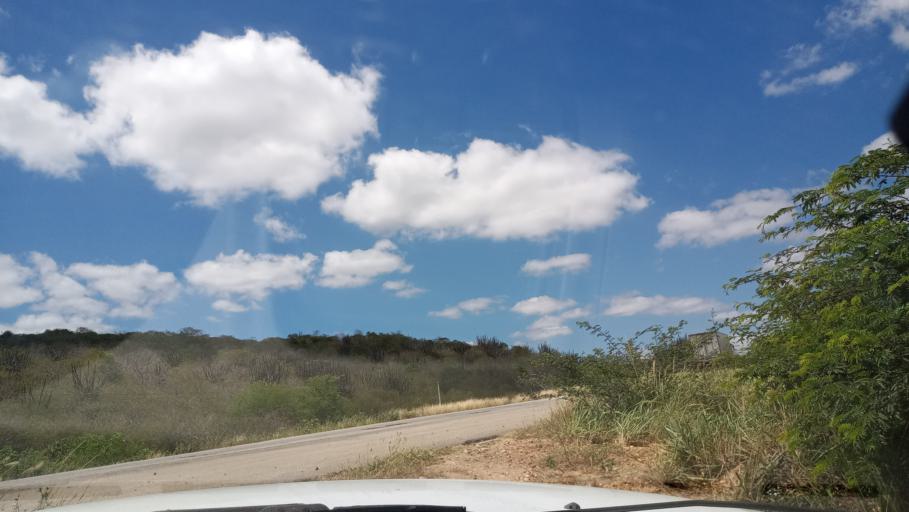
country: BR
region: Rio Grande do Norte
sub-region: Sao Paulo Do Potengi
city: Sao Paulo do Potengi
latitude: -5.7483
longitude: -35.9083
